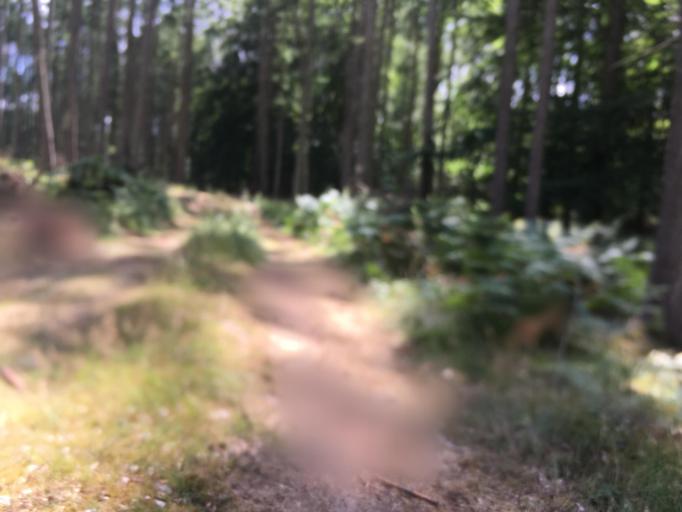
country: DE
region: Brandenburg
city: Althuttendorf
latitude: 52.9436
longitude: 13.7715
